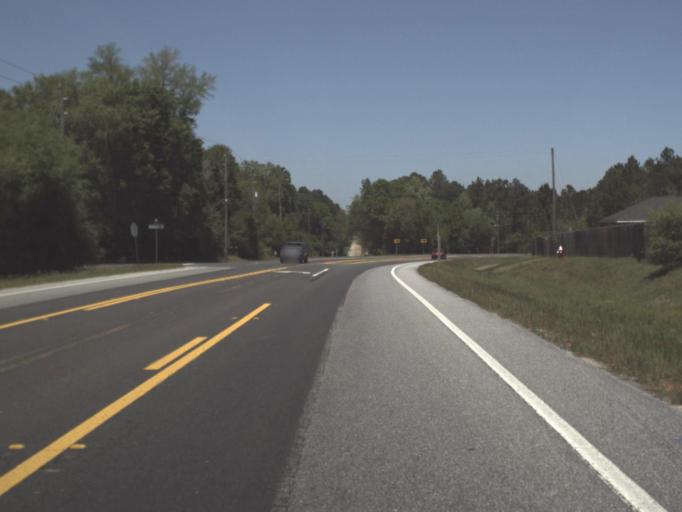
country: US
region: Florida
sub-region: Escambia County
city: Bellview
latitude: 30.4828
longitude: -87.3234
